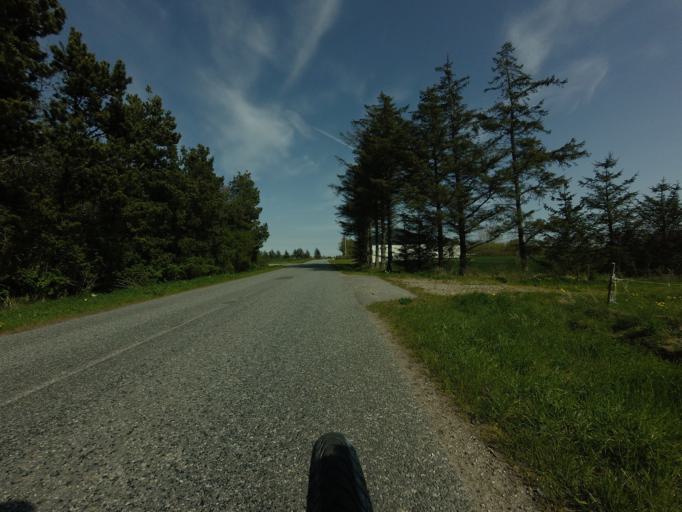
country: DK
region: North Denmark
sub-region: Jammerbugt Kommune
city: Pandrup
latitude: 57.2257
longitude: 9.6467
